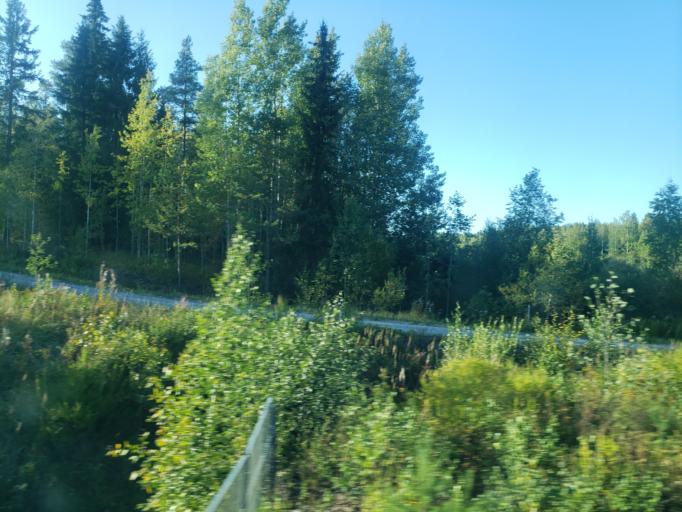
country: FI
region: South Karelia
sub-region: Lappeenranta
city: Lappeenranta
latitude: 60.9105
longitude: 28.1660
